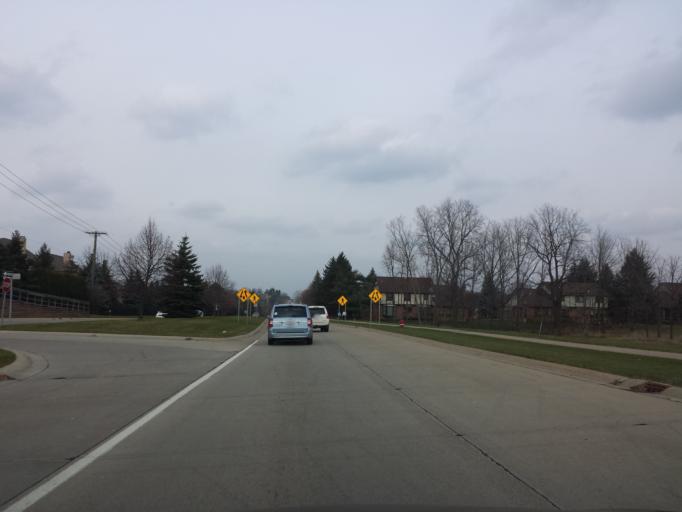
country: US
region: Michigan
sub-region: Oakland County
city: Rochester Hills
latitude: 42.6494
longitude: -83.1925
